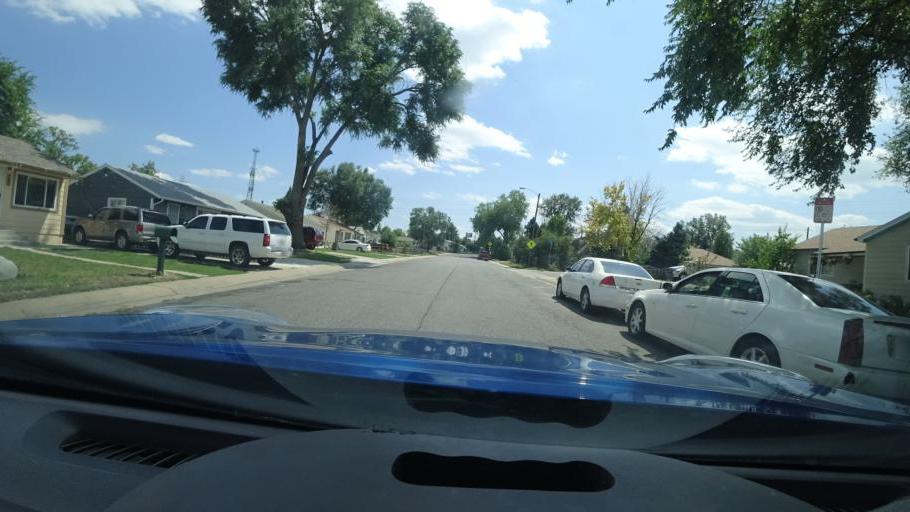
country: US
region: Colorado
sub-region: Jefferson County
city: Lakewood
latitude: 39.7027
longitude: -105.0484
